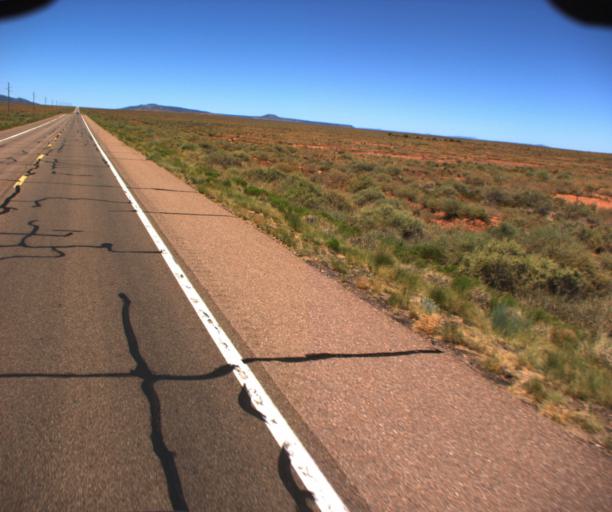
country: US
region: Arizona
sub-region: Coconino County
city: LeChee
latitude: 34.9576
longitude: -110.7495
